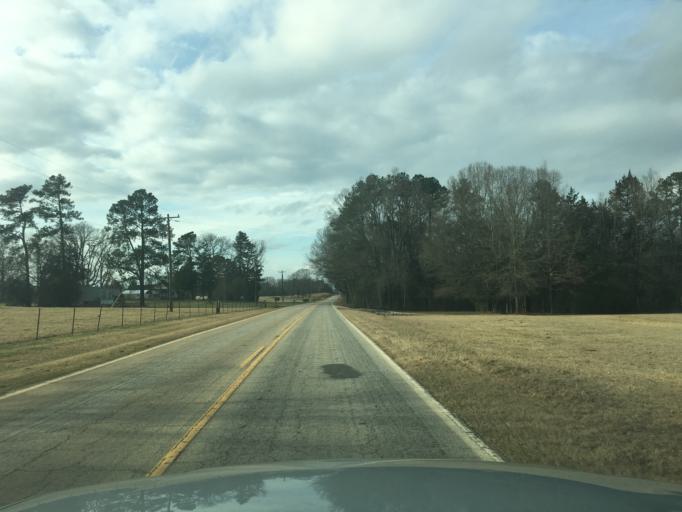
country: US
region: South Carolina
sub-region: Abbeville County
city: Due West
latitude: 34.3370
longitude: -82.4872
